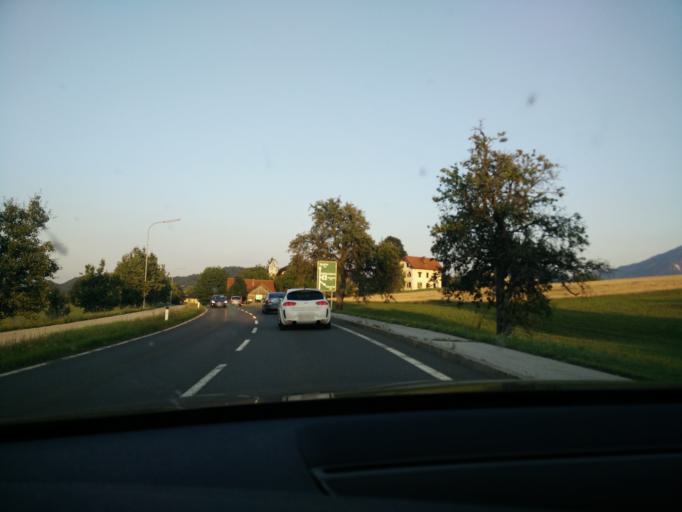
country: AT
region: Carinthia
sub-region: Politischer Bezirk Villach Land
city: Wernberg
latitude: 46.5876
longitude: 13.9105
